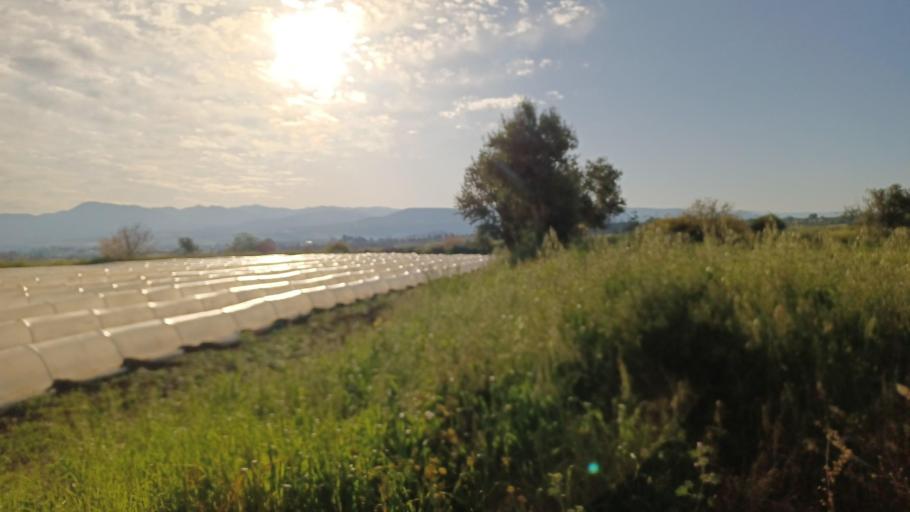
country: CY
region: Pafos
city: Polis
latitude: 35.0291
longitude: 32.3989
